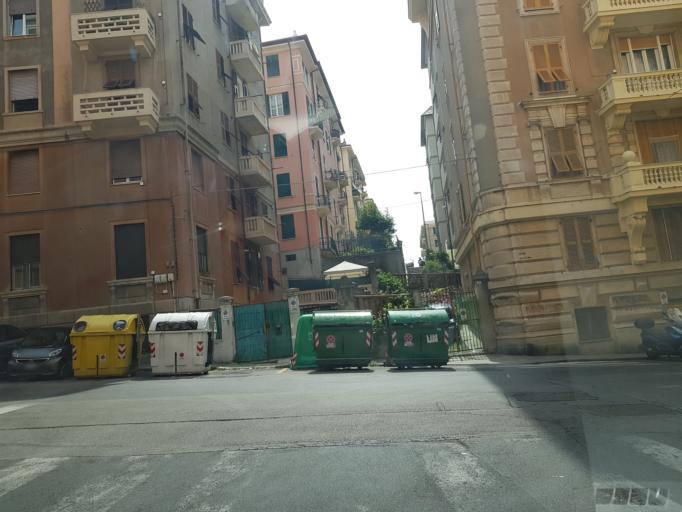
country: IT
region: Liguria
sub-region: Provincia di Genova
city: San Teodoro
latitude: 44.4277
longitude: 8.8473
